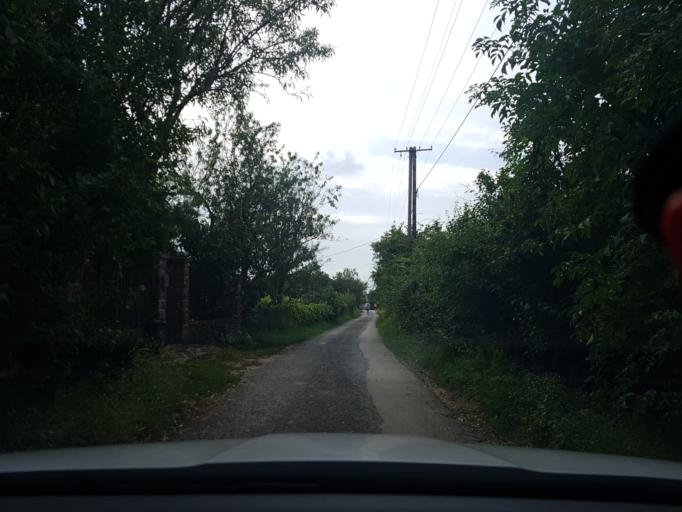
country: HU
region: Veszprem
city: Balatonalmadi
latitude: 46.9913
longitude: 17.9808
